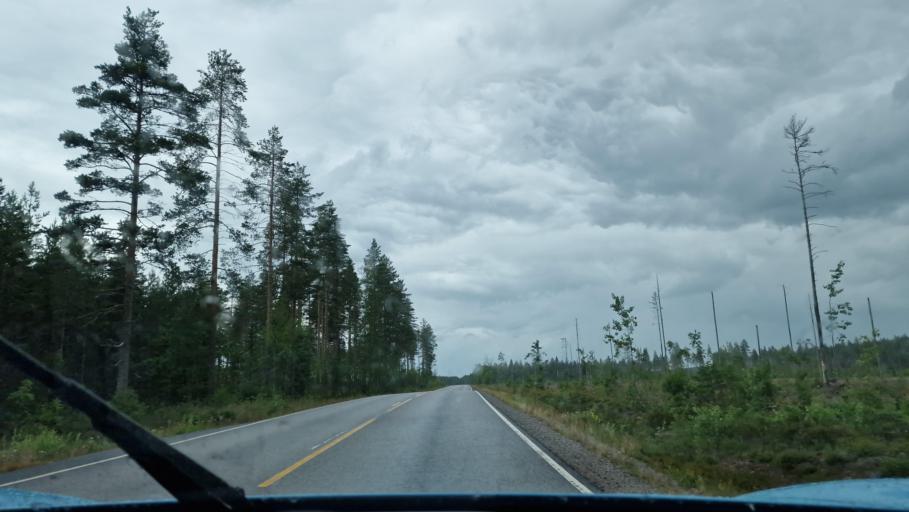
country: FI
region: Central Finland
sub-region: Saarijaervi-Viitasaari
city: Pylkoenmaeki
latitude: 62.6000
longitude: 24.5867
